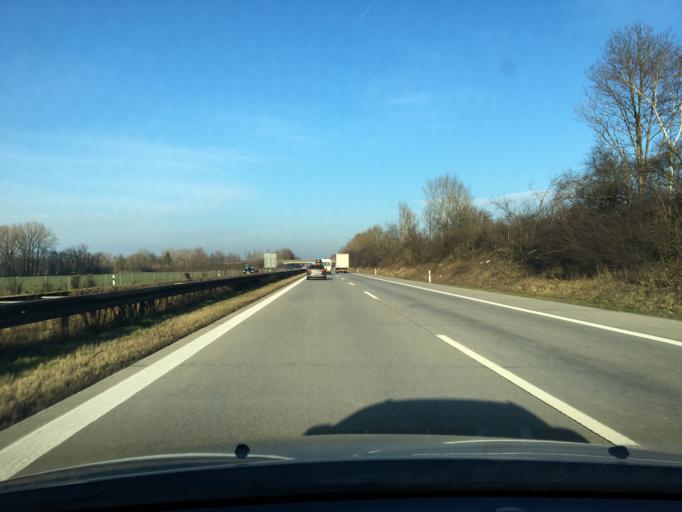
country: DE
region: Bavaria
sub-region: Upper Bavaria
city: Langenpreising
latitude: 48.4534
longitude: 11.9691
